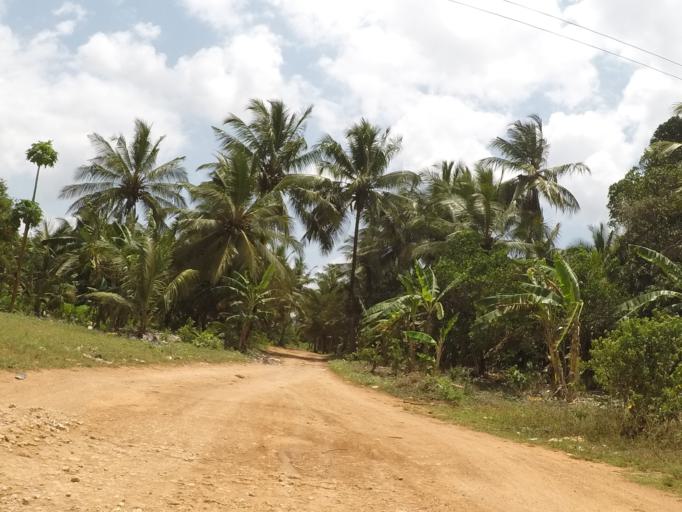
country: TZ
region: Zanzibar Central/South
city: Koani
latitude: -6.1848
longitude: 39.3108
